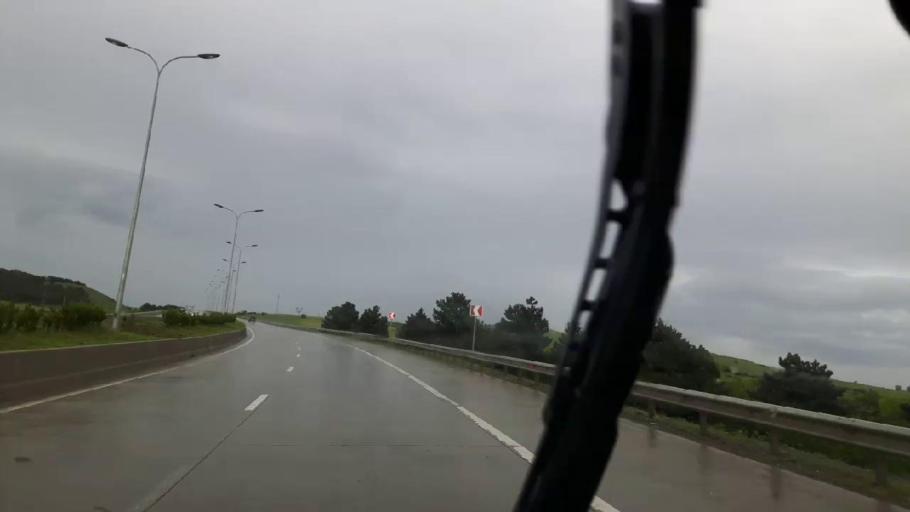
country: GE
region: Shida Kartli
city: Gori
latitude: 42.0201
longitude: 44.0031
